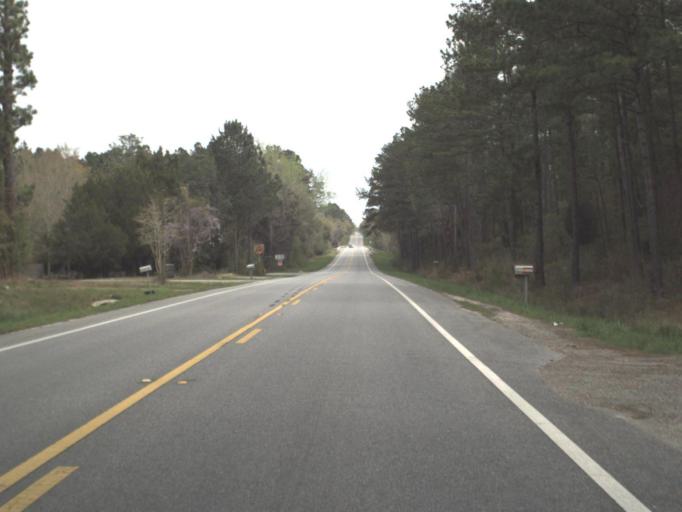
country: US
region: Florida
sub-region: Holmes County
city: Bonifay
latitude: 30.8749
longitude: -85.6631
